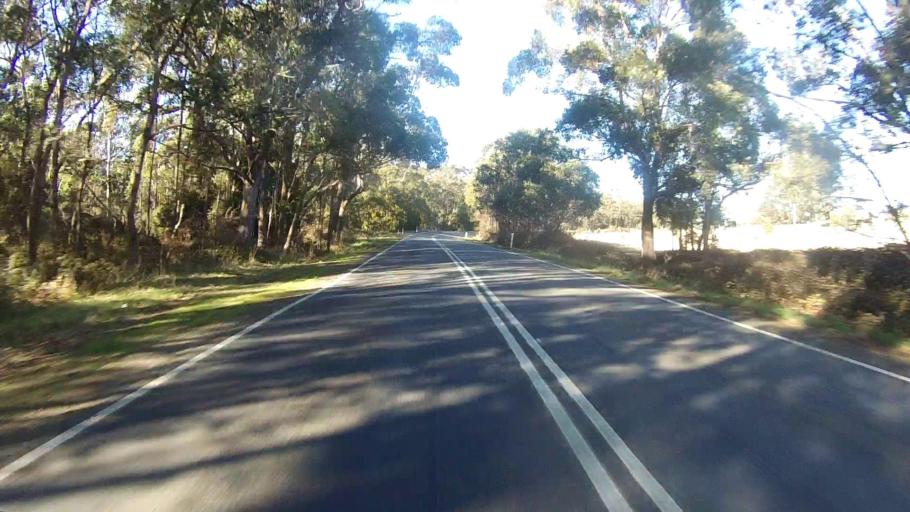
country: AU
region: Tasmania
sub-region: Sorell
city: Sorell
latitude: -42.8228
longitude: 147.8041
